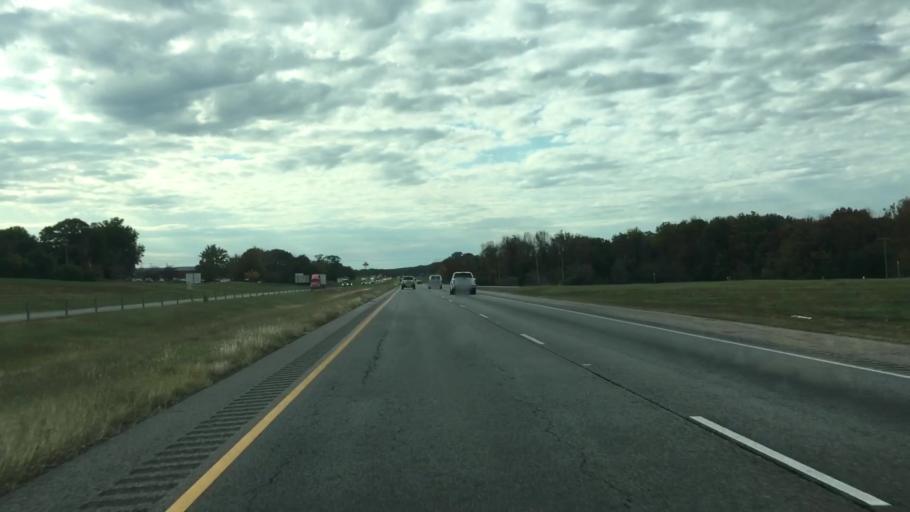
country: US
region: Arkansas
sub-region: Conway County
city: Morrilton
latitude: 35.1743
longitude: -92.7207
